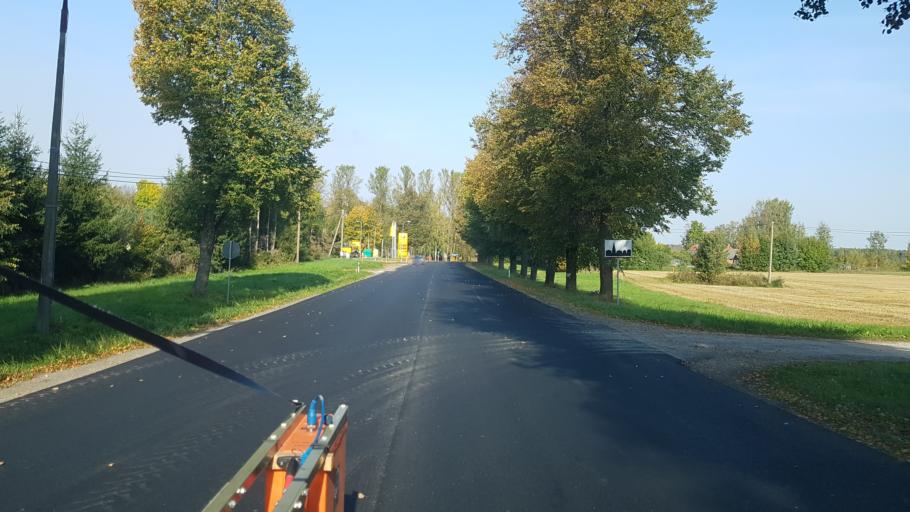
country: EE
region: Polvamaa
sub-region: Polva linn
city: Polva
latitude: 58.2047
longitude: 27.0754
